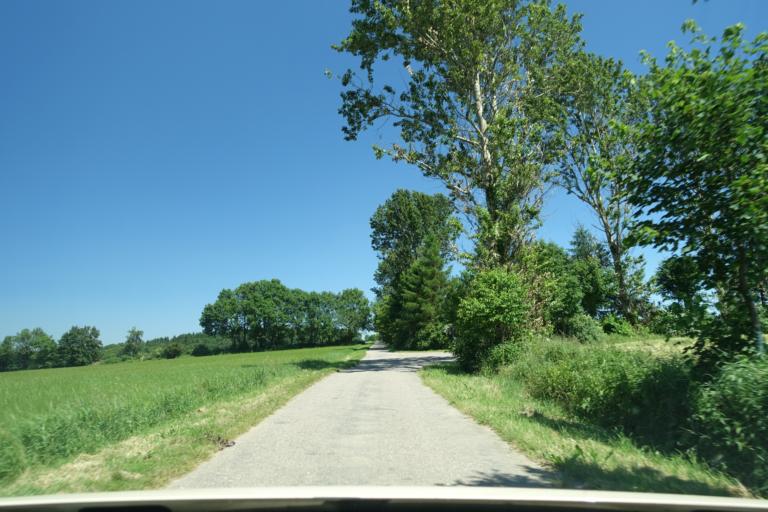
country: DE
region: Saxony
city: Eppendorf
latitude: 50.8238
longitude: 13.2551
